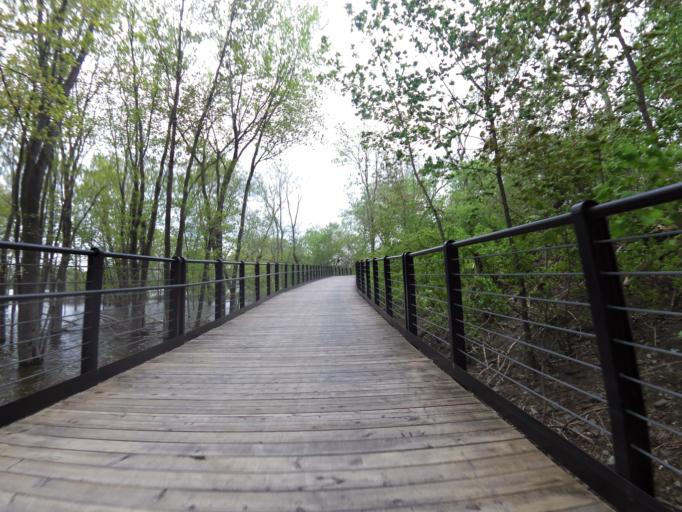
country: CA
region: Ontario
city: Ottawa
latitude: 45.4356
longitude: -75.7073
